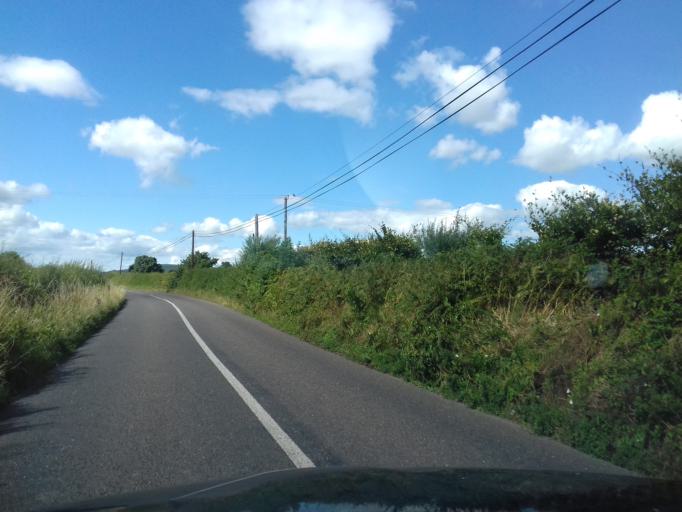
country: IE
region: Munster
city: Carrick-on-Suir
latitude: 52.3608
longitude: -7.4314
